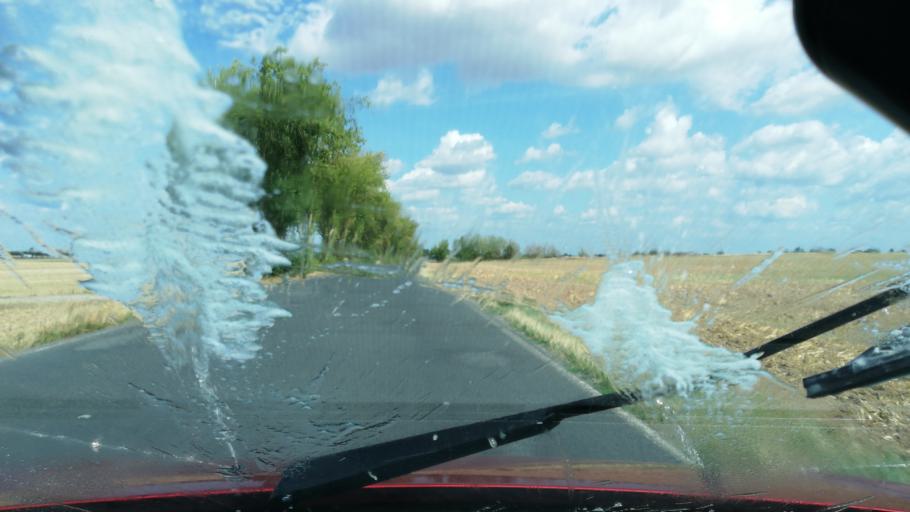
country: DE
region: Saxony-Anhalt
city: Landsberg
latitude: 51.5269
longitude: 12.1360
